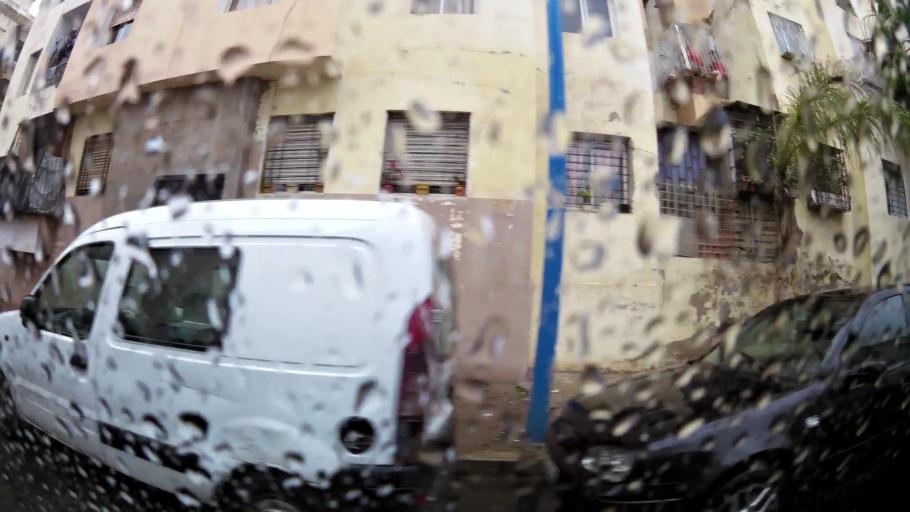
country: MA
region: Grand Casablanca
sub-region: Casablanca
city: Casablanca
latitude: 33.5566
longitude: -7.6700
